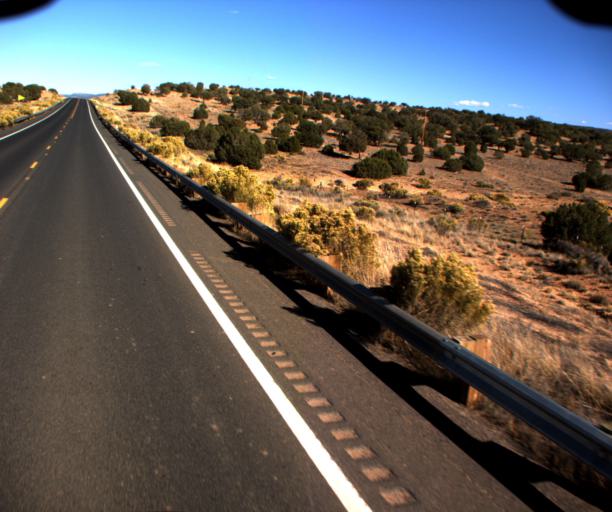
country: US
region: Arizona
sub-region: Coconino County
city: Kaibito
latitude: 36.4491
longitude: -110.7208
